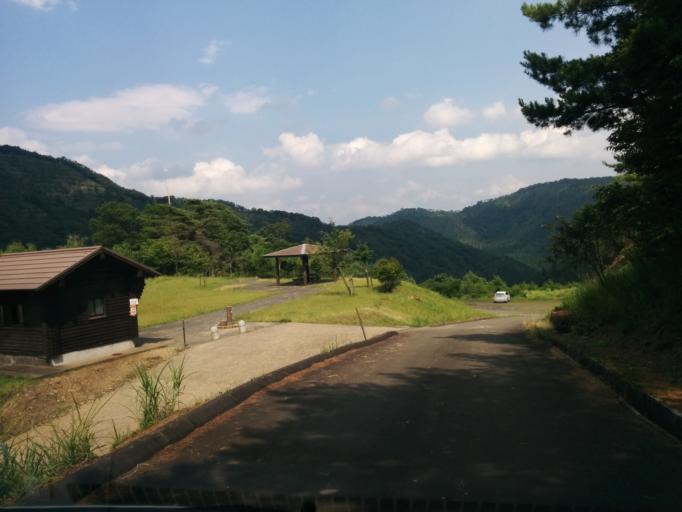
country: JP
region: Kyoto
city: Miyazu
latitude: 35.4598
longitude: 135.1377
